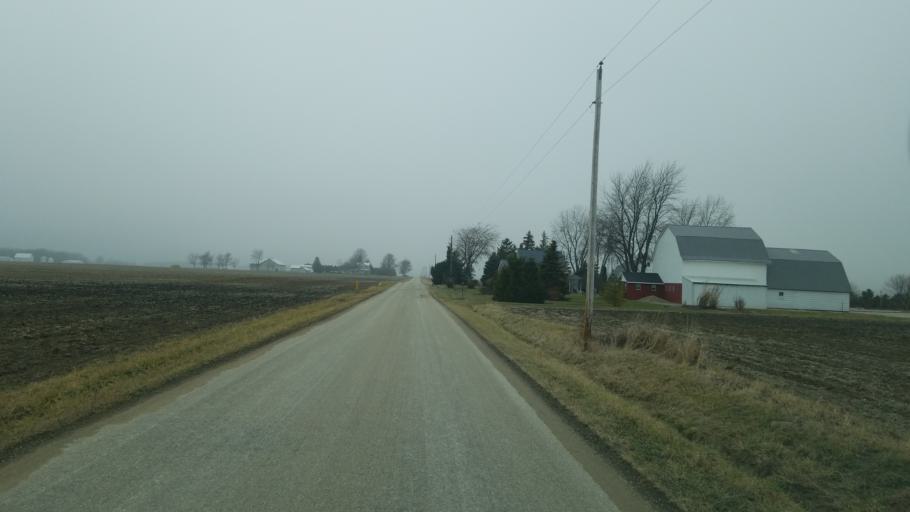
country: US
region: Indiana
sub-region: Adams County
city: Geneva
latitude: 40.5762
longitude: -85.0297
